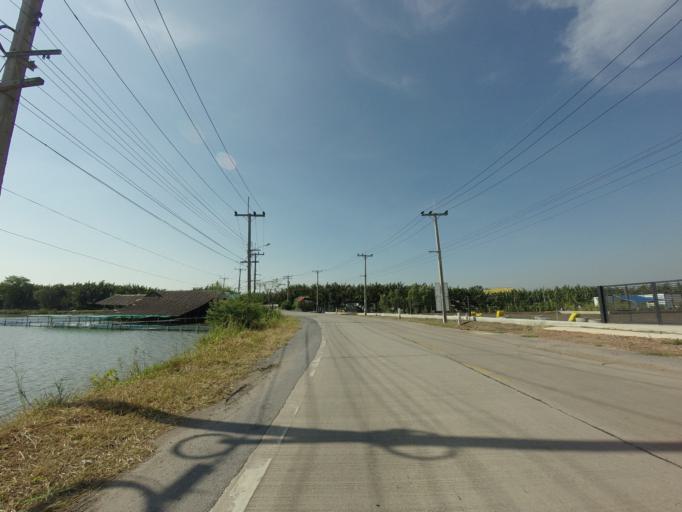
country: TH
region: Samut Prakan
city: Phra Samut Chedi
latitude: 13.5565
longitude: 100.5370
